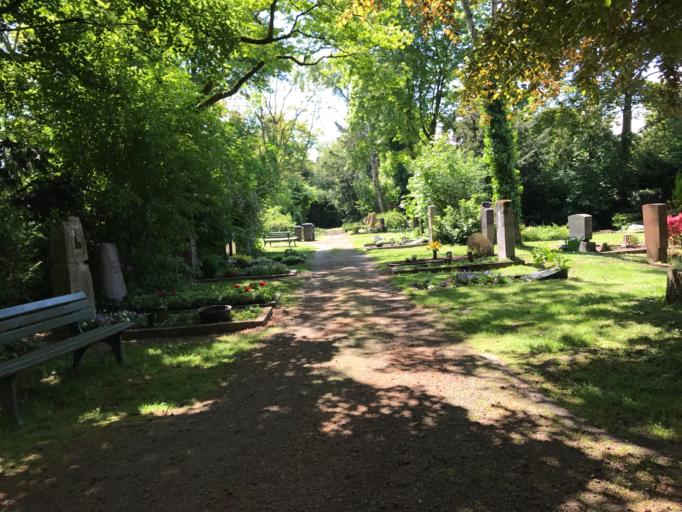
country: DE
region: North Rhine-Westphalia
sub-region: Regierungsbezirk Dusseldorf
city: Neuss
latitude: 51.2355
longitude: 6.7166
